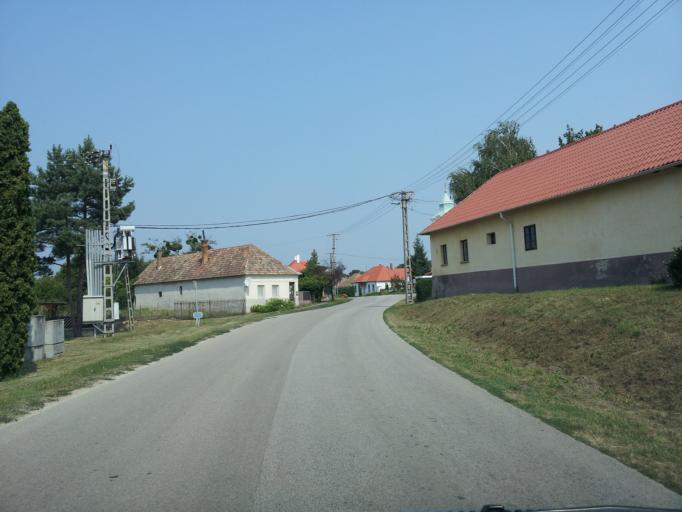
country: HU
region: Gyor-Moson-Sopron
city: Bakonyszentlaszlo
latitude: 47.4176
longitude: 17.8045
